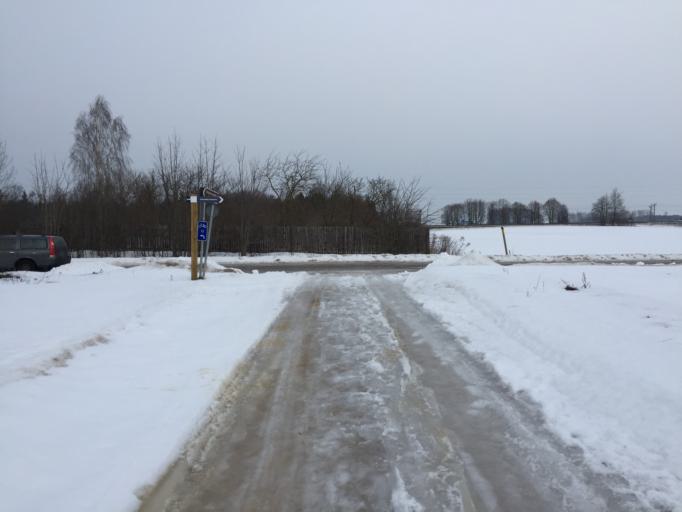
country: LV
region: Ikskile
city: Ikskile
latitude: 56.8449
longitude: 24.4529
